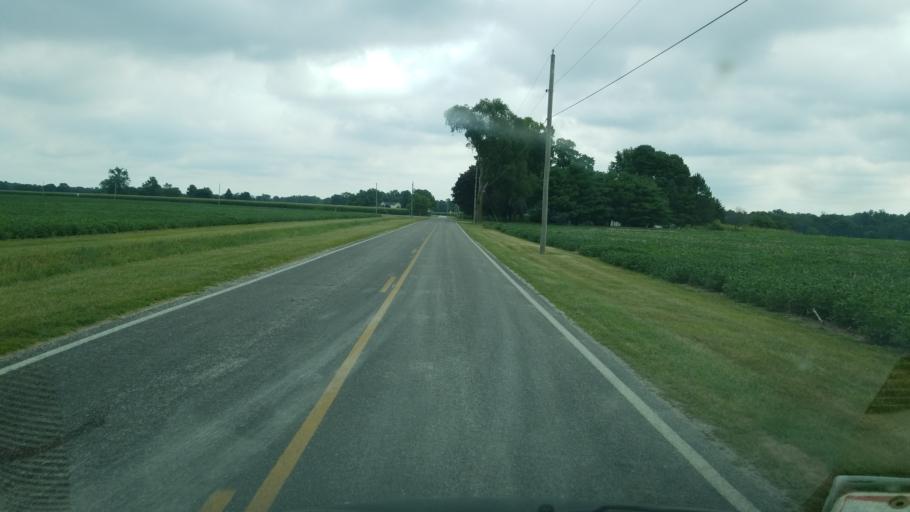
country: US
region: Ohio
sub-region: Sandusky County
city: Green Springs
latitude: 41.2124
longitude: -83.1406
